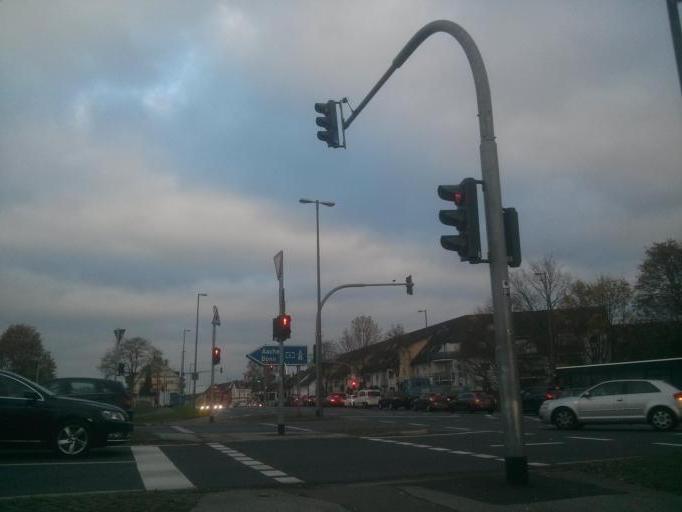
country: DE
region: North Rhine-Westphalia
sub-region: Regierungsbezirk Koln
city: Poll
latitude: 50.9106
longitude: 7.0020
